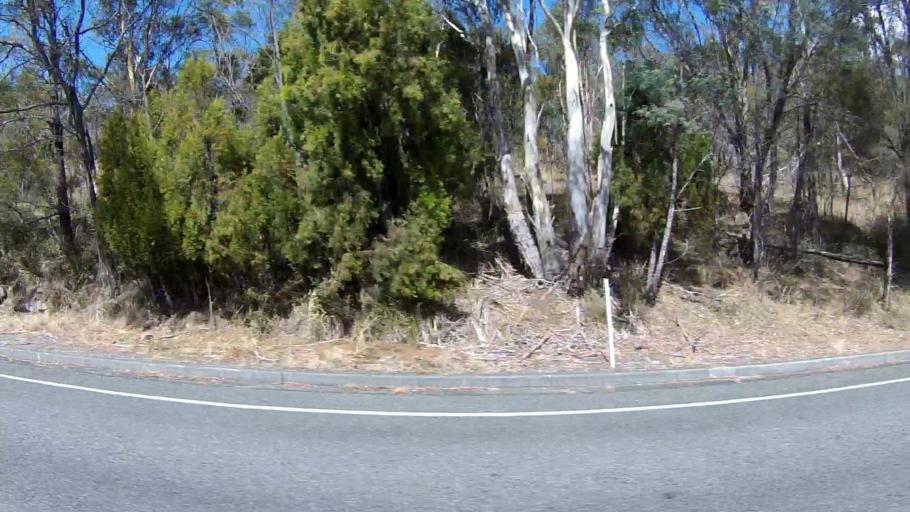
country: AU
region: Tasmania
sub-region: Sorell
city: Sorell
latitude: -42.6072
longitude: 147.6807
